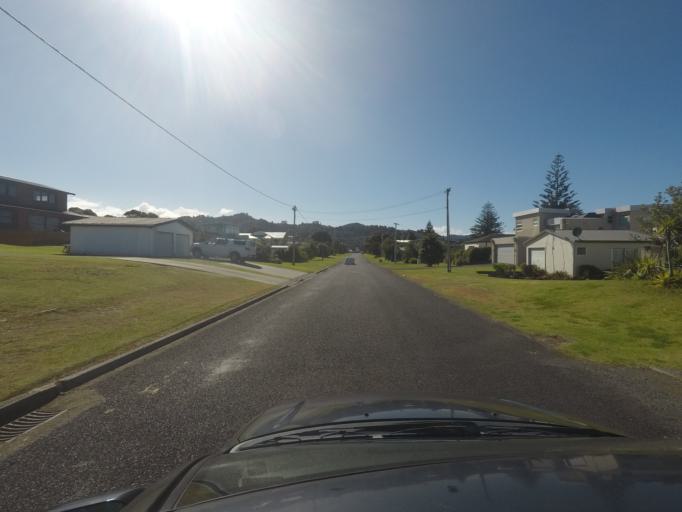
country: NZ
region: Bay of Plenty
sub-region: Western Bay of Plenty District
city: Waihi Beach
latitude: -37.4081
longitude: 175.9444
